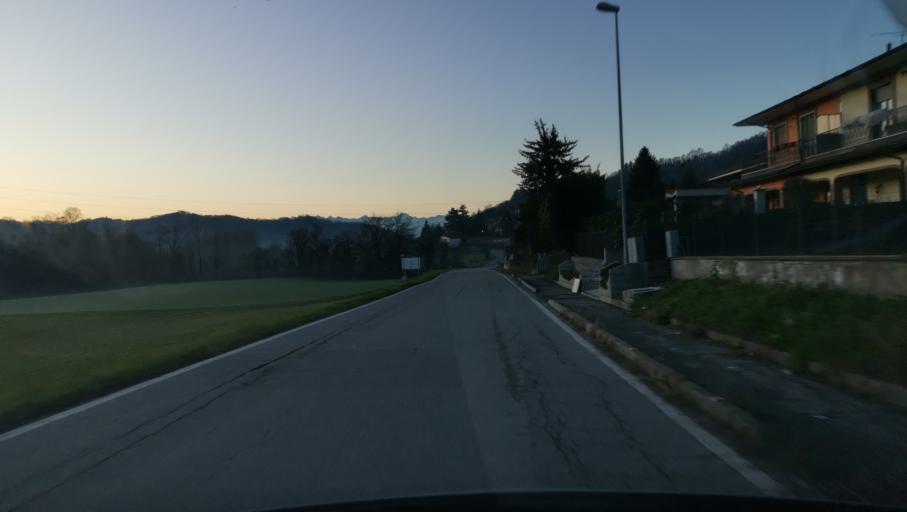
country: IT
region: Piedmont
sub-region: Provincia di Torino
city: Rivalba
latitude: 45.1124
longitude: 7.8813
